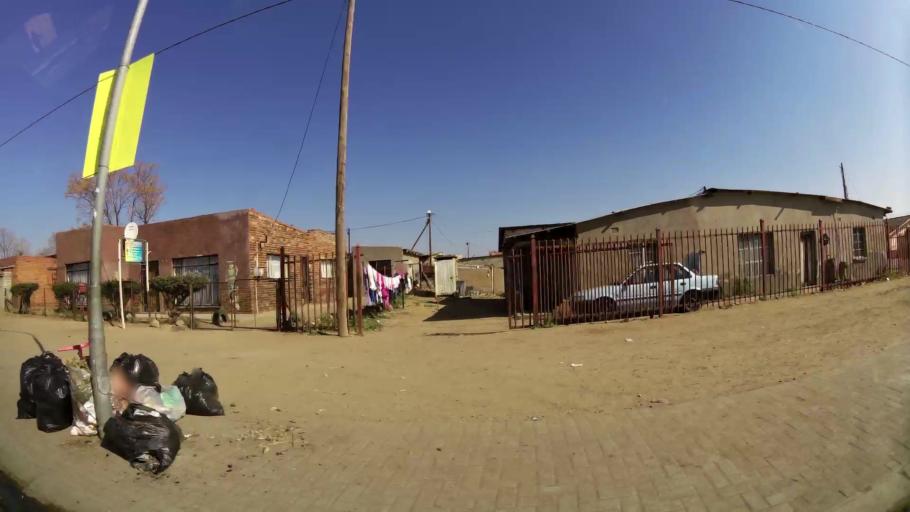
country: ZA
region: Orange Free State
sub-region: Mangaung Metropolitan Municipality
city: Bloemfontein
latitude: -29.1528
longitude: 26.2408
